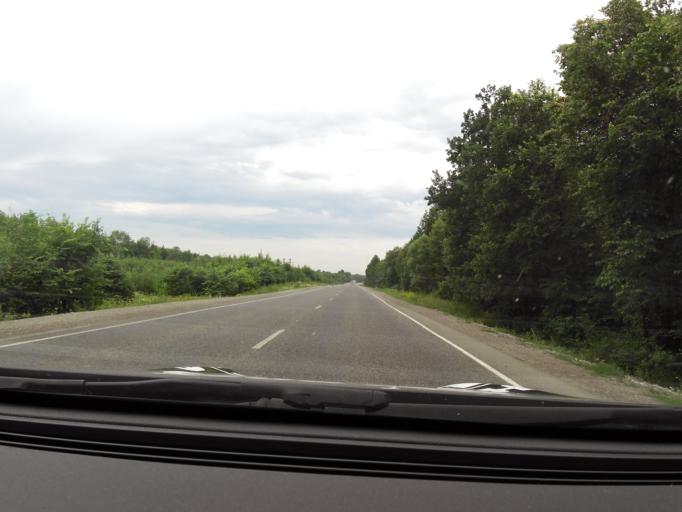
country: RU
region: Bashkortostan
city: Ulu-Telyak
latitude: 54.8343
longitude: 56.9984
